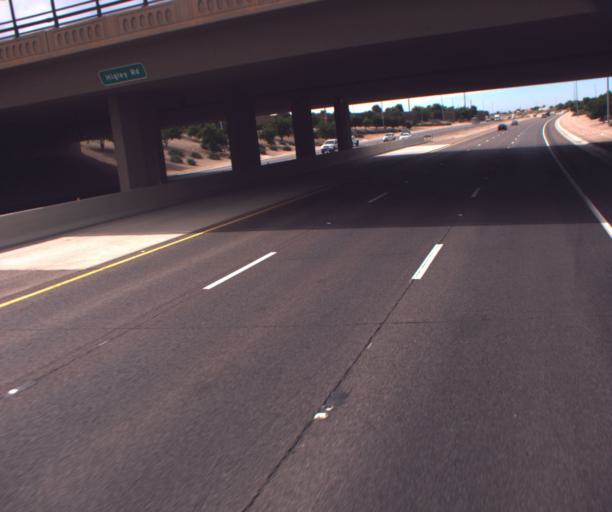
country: US
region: Arizona
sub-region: Maricopa County
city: Gilbert
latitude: 33.3280
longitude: -111.7208
